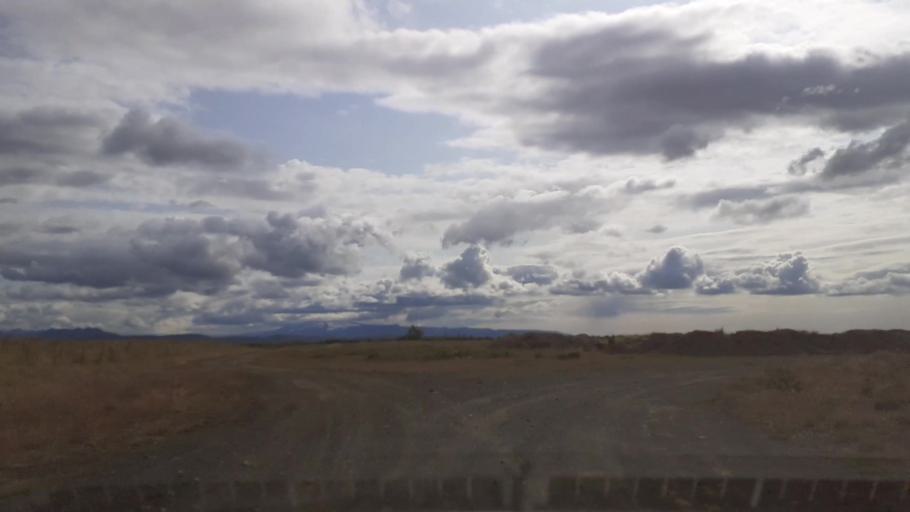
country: IS
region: South
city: Vestmannaeyjar
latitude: 63.8286
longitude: -20.4015
